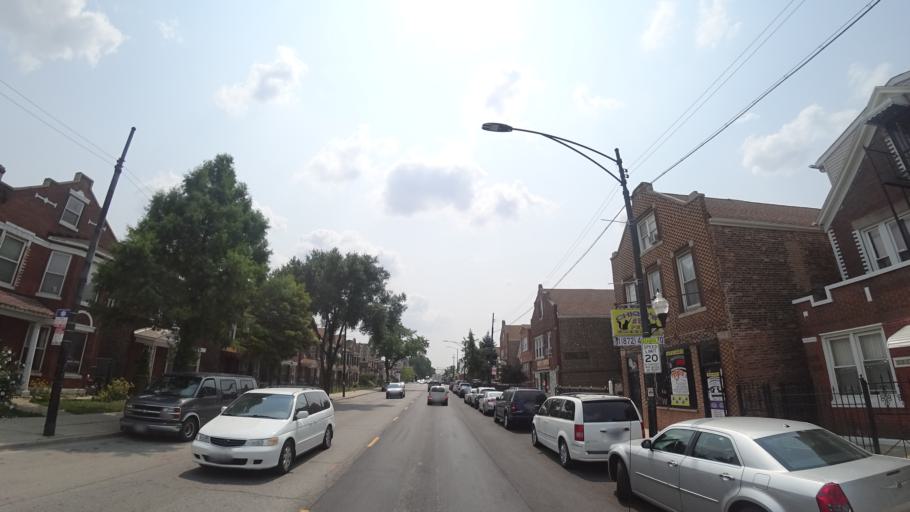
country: US
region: Illinois
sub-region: Cook County
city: Cicero
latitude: 41.8381
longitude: -87.7244
